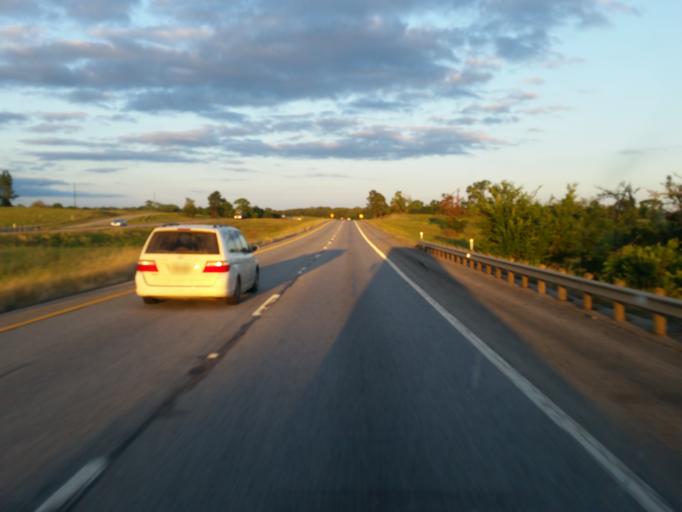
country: US
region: Texas
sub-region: Van Zandt County
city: Van
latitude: 32.5038
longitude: -95.6324
